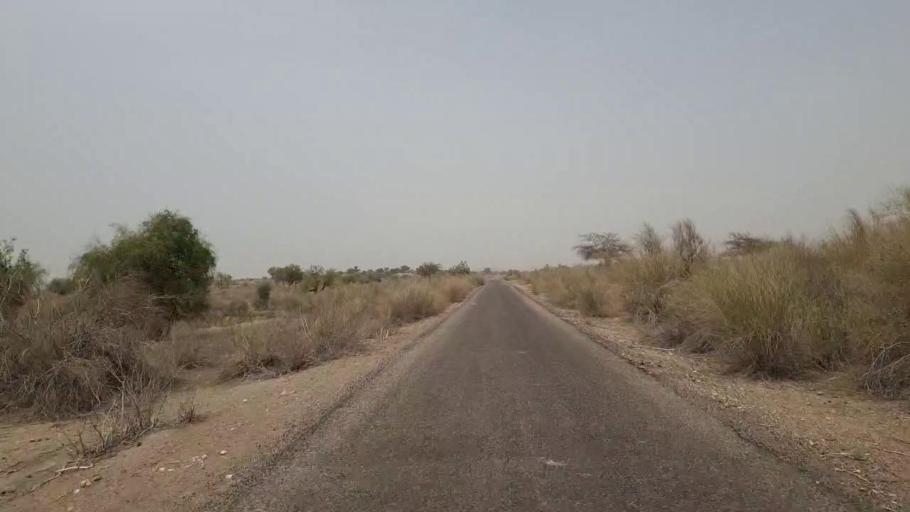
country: PK
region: Sindh
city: Islamkot
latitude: 24.7831
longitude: 70.5030
